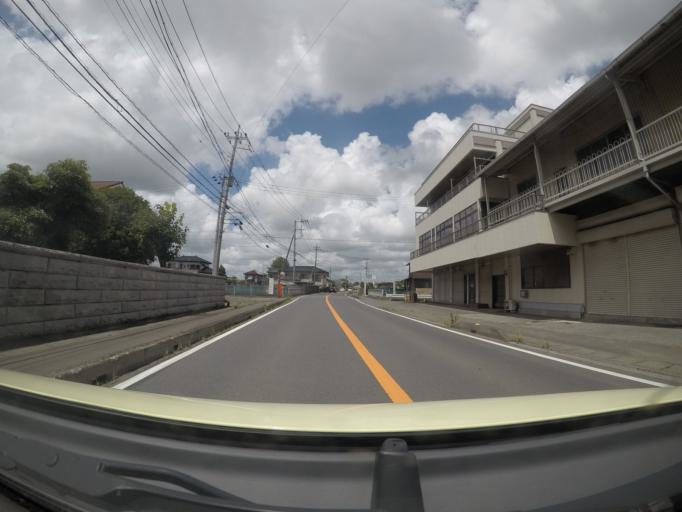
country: JP
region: Ibaraki
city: Mitsukaido
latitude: 36.0385
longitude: 139.9878
